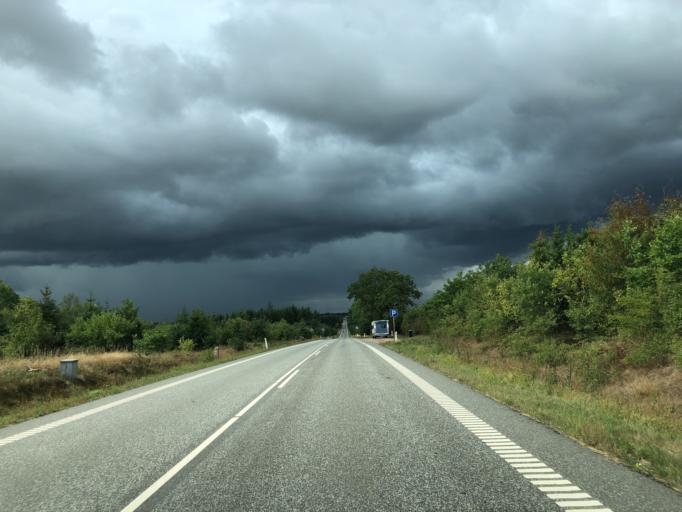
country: DK
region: Central Jutland
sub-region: Ikast-Brande Kommune
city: Bording Kirkeby
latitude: 56.1381
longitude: 9.3853
